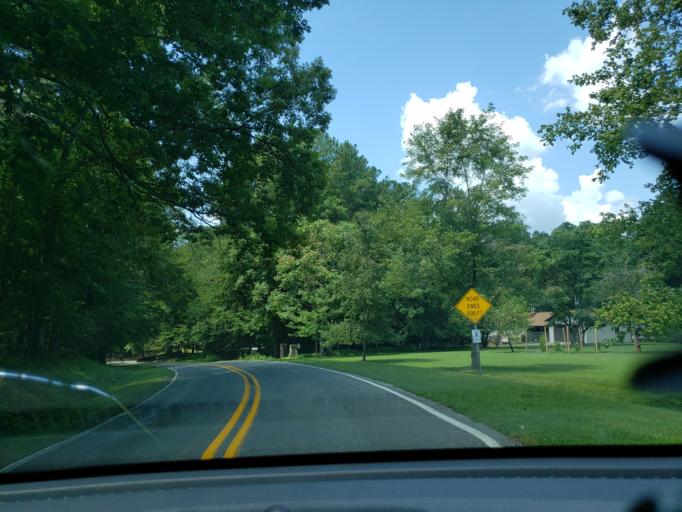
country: US
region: North Carolina
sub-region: Orange County
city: Hillsborough
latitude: 36.0786
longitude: -79.0020
